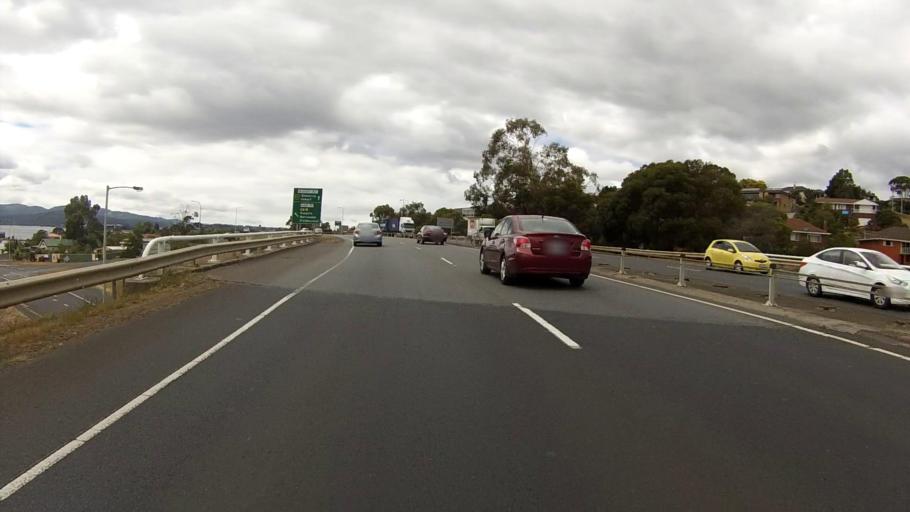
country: AU
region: Tasmania
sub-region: Glenorchy
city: Berriedale
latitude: -42.8148
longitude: 147.2523
